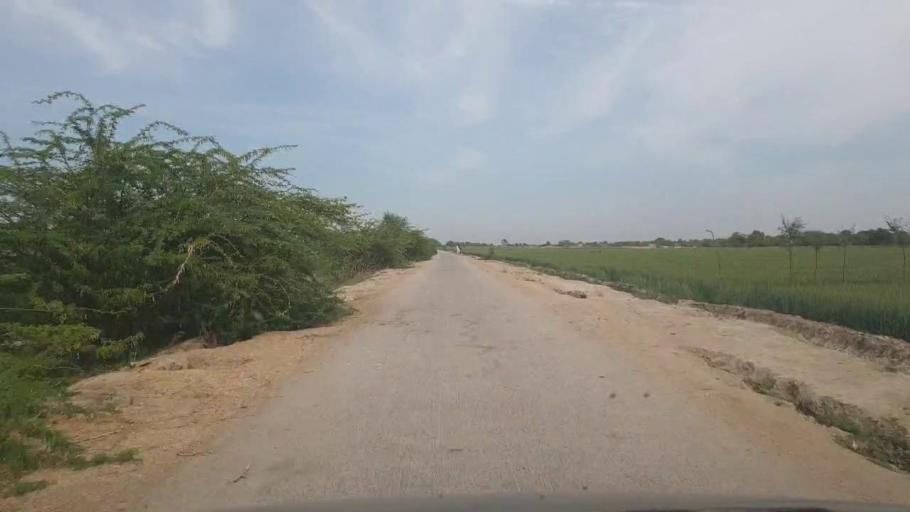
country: PK
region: Sindh
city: Kunri
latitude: 25.2511
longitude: 69.6245
